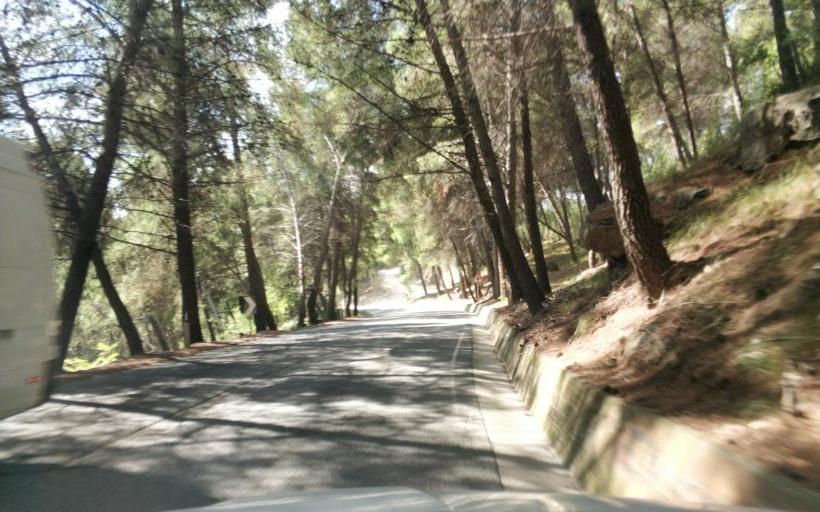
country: AL
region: Durres
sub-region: Rrethi i Krujes
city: Kruje
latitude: 41.4946
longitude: 19.7736
